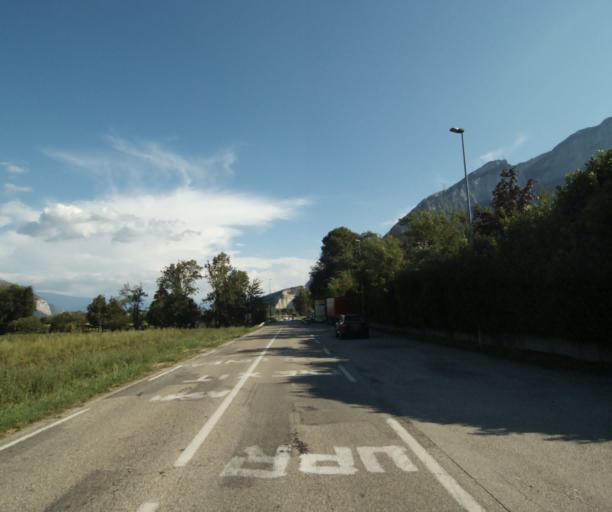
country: FR
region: Rhone-Alpes
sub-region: Departement de l'Isere
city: Noyarey
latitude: 45.2511
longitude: 5.6309
